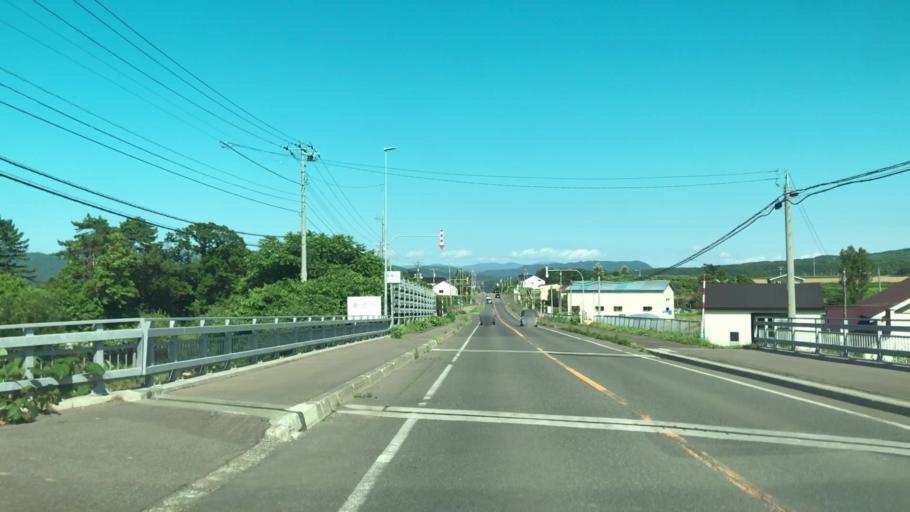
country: JP
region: Hokkaido
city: Iwanai
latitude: 42.9805
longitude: 140.5919
